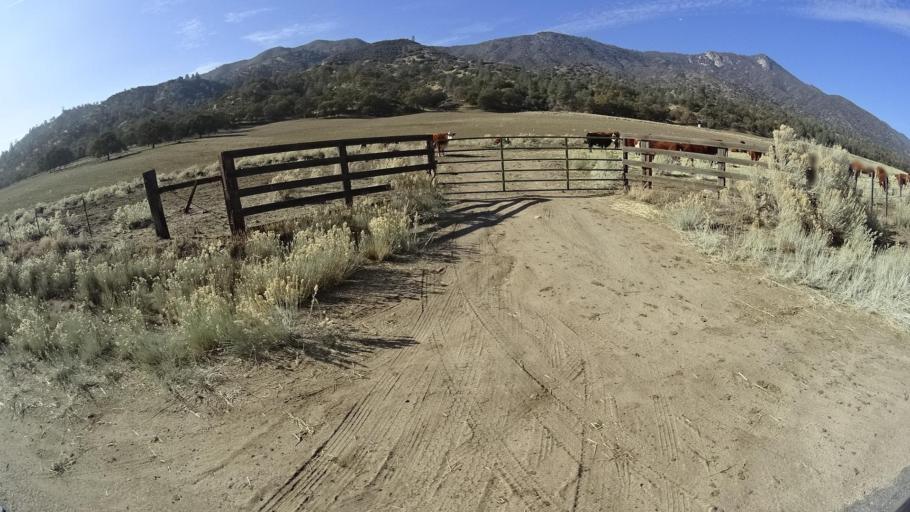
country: US
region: California
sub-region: Kern County
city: Bodfish
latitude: 35.4010
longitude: -118.5449
